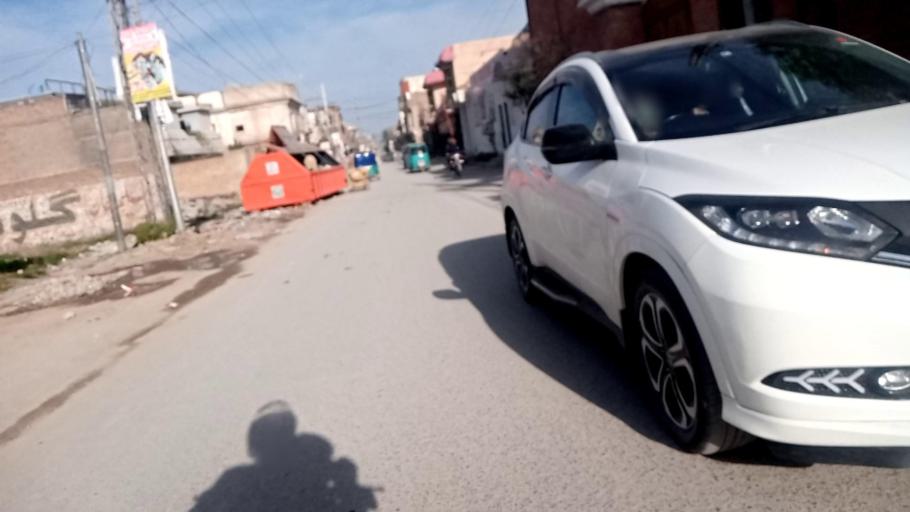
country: PK
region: Khyber Pakhtunkhwa
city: Peshawar
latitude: 34.0117
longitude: 71.6077
